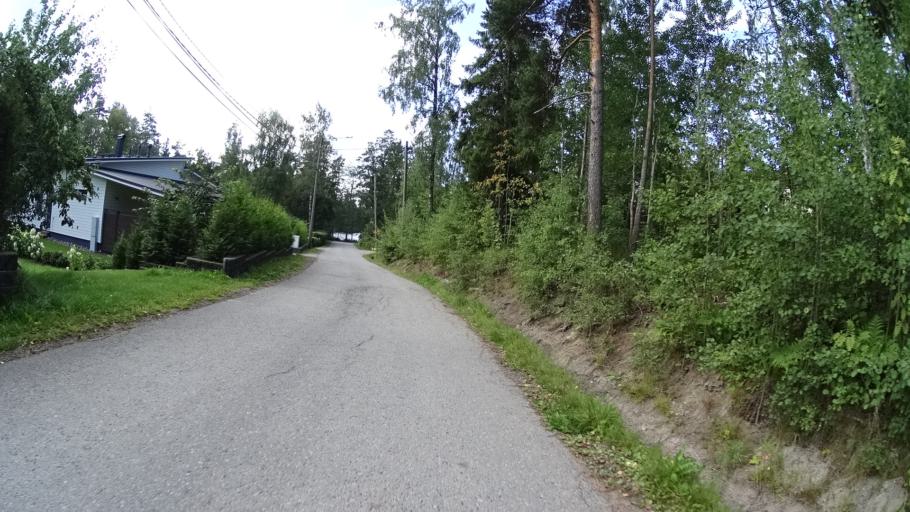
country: FI
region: Uusimaa
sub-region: Helsinki
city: Kauniainen
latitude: 60.2222
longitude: 24.7355
